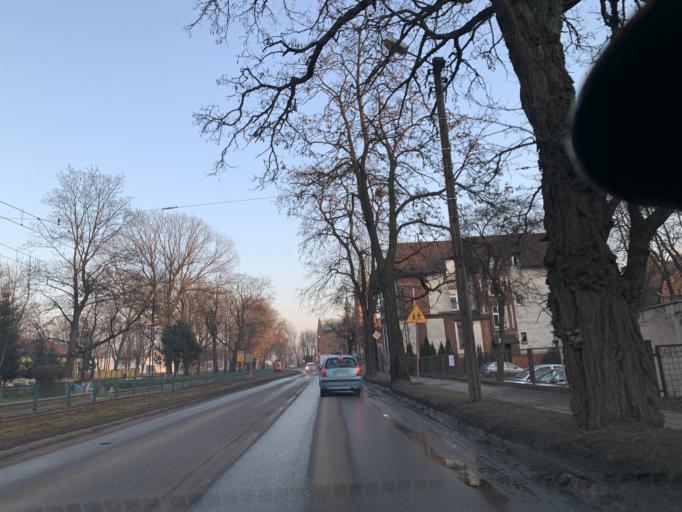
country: PL
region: Silesian Voivodeship
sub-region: Bytom
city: Bytom
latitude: 50.3372
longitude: 18.8933
